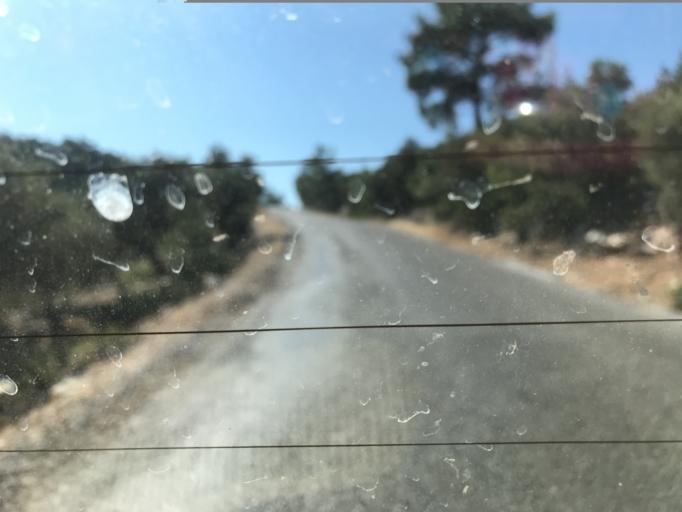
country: TR
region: Mugla
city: Selimiye
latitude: 37.3869
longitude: 27.4826
